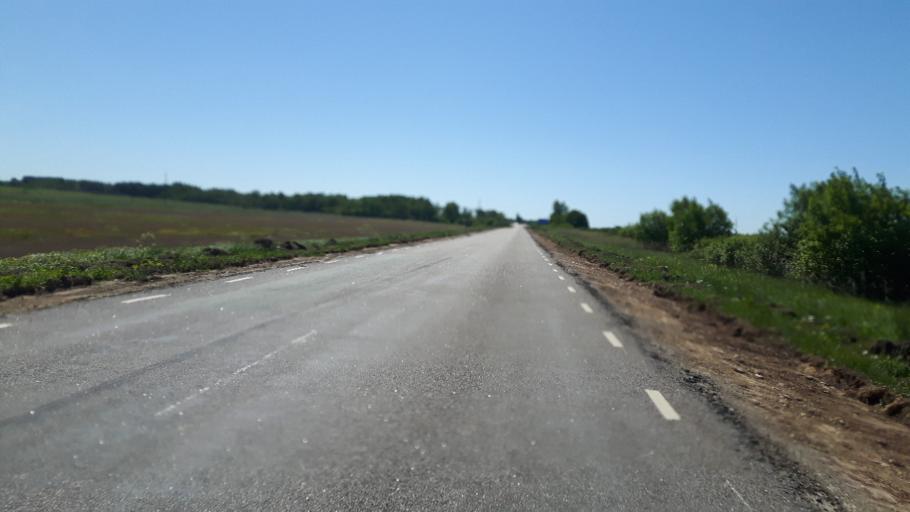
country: EE
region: Ida-Virumaa
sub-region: Narva-Joesuu linn
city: Narva-Joesuu
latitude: 59.3847
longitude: 27.9207
